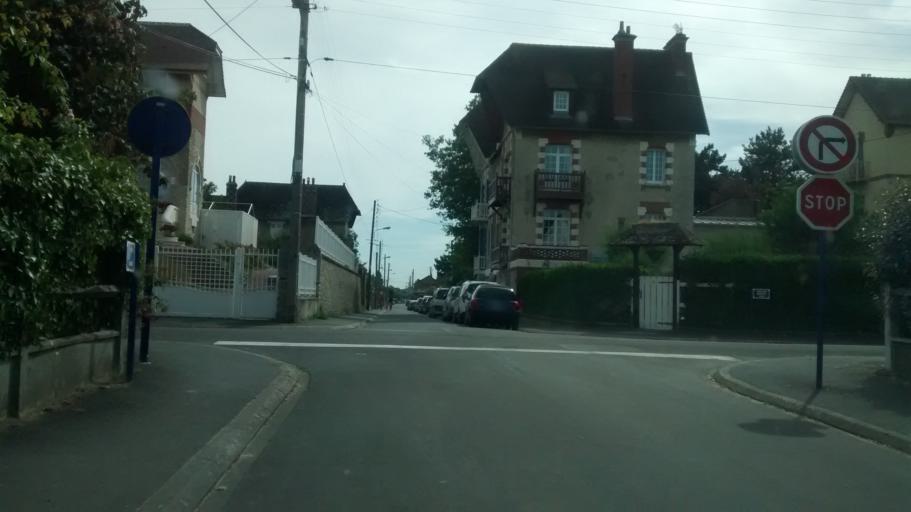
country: FR
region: Lower Normandy
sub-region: Departement du Calvados
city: Ouistreham
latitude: 49.2903
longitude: -0.2664
